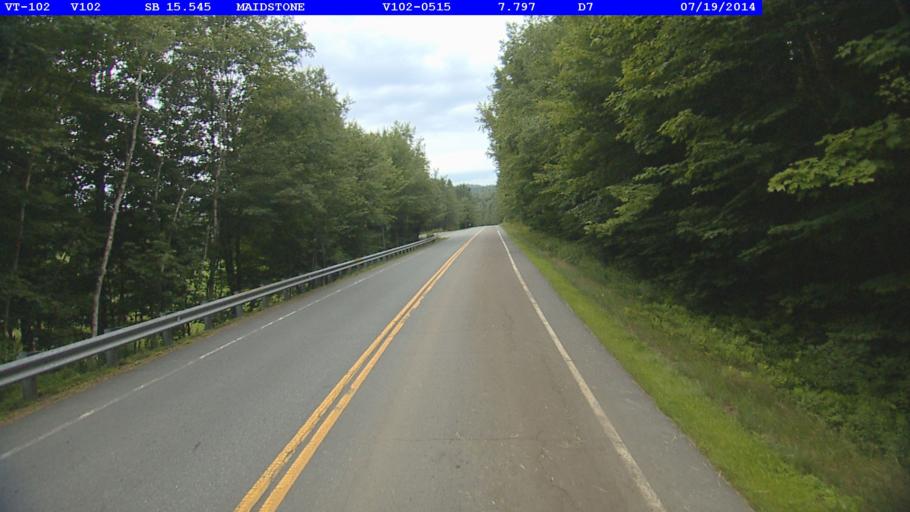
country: US
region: New Hampshire
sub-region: Coos County
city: Stratford
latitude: 44.6623
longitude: -71.5907
